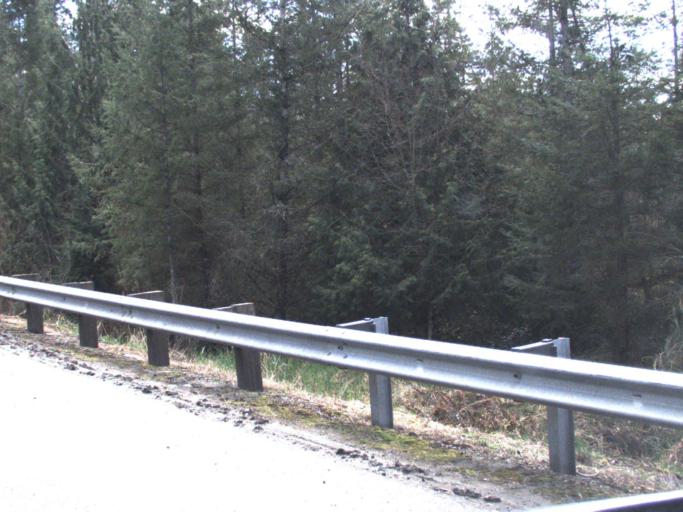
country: US
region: Washington
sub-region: King County
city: Black Diamond
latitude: 47.3347
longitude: -122.0126
